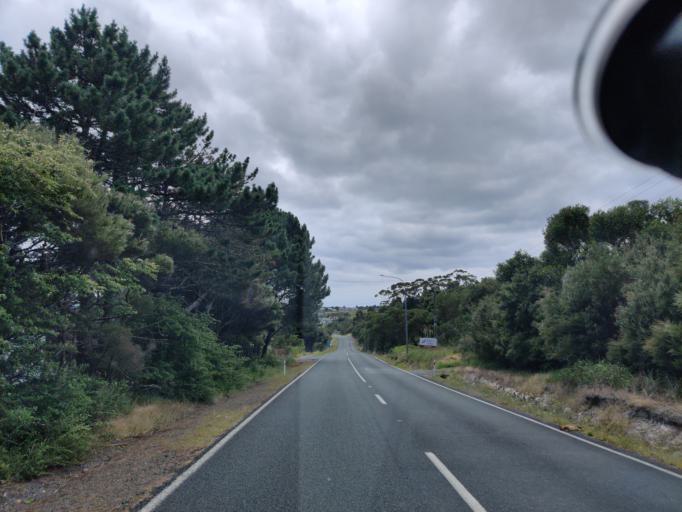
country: NZ
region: Northland
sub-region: Far North District
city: Kaitaia
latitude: -34.6559
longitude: 172.9686
